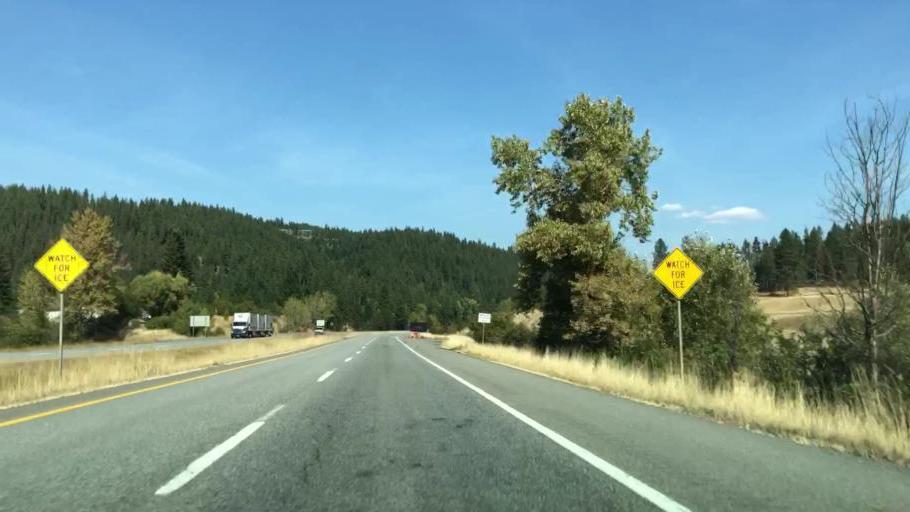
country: US
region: Idaho
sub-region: Shoshone County
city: Pinehurst
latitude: 47.5494
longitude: -116.3208
